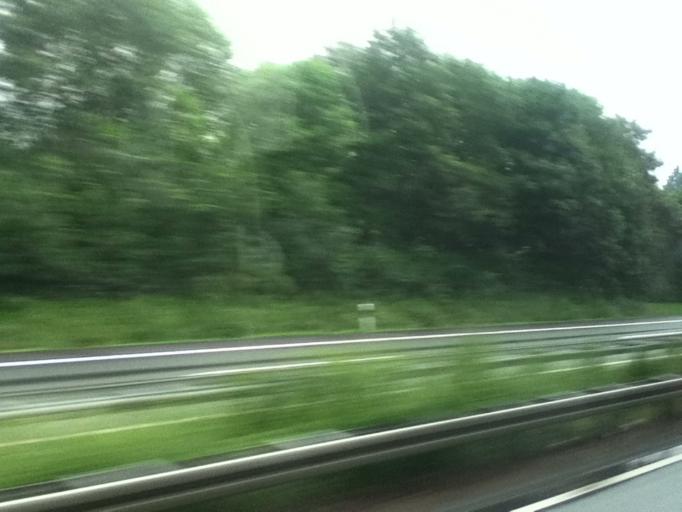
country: DE
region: North Rhine-Westphalia
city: Wiehl
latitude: 50.9711
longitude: 7.5500
